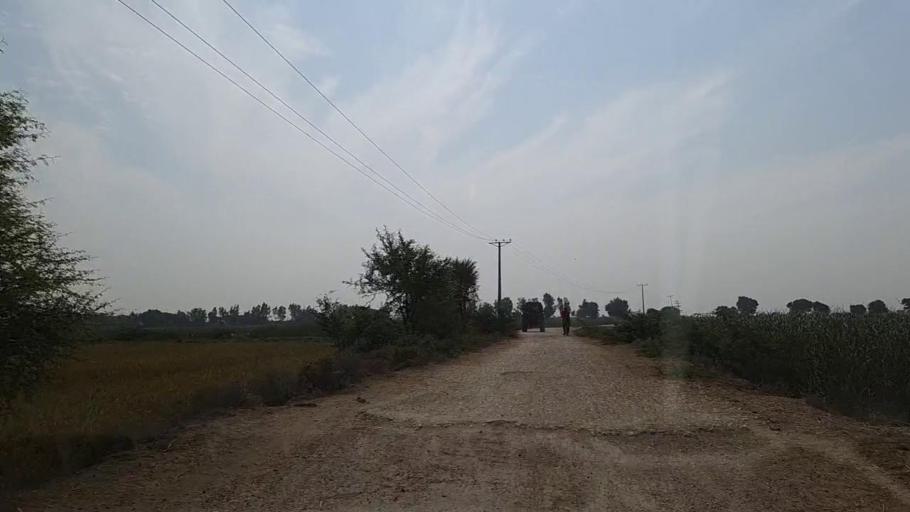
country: PK
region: Sindh
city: Mirpur Batoro
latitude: 24.6142
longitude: 68.2364
